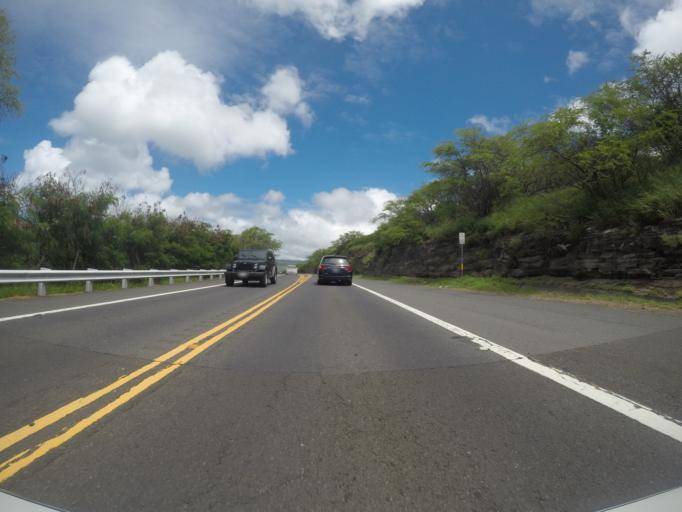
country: US
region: Hawaii
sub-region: Honolulu County
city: Waimanalo Beach
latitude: 21.2745
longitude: -157.6912
